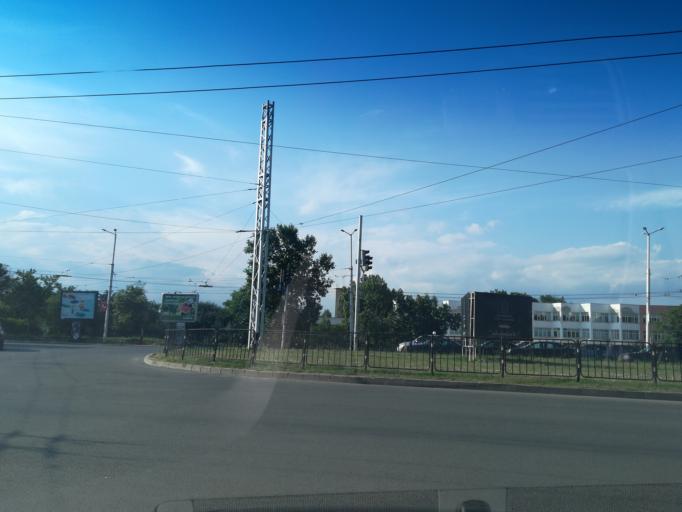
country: BG
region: Plovdiv
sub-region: Obshtina Plovdiv
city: Plovdiv
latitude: 42.1488
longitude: 24.7794
